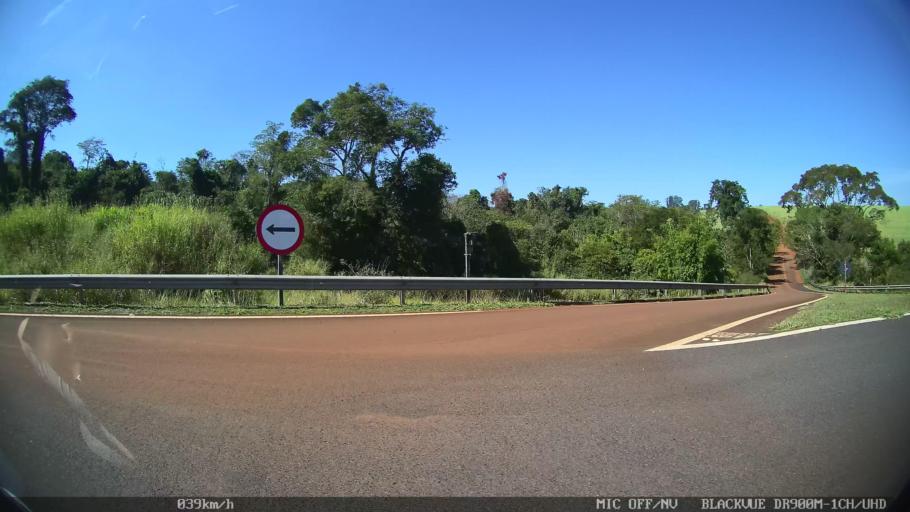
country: BR
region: Sao Paulo
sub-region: Franca
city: Franca
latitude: -20.6339
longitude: -47.4683
